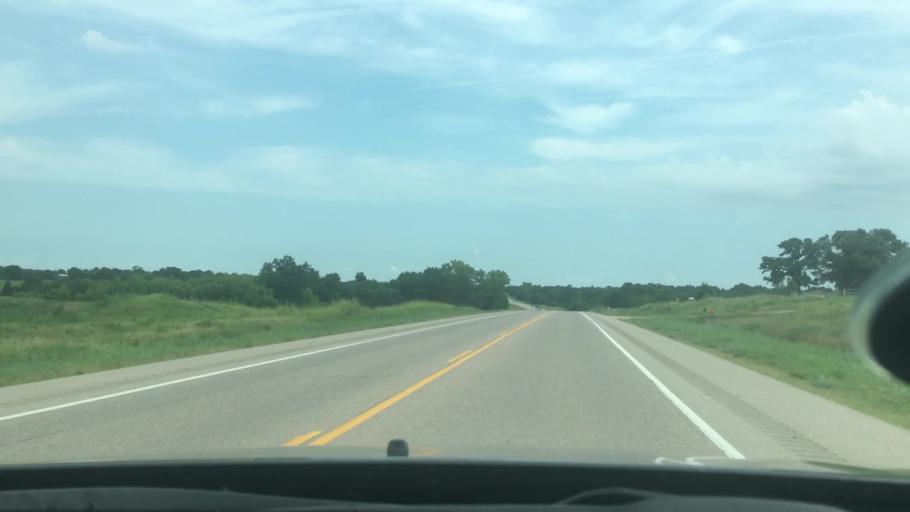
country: US
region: Oklahoma
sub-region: Seminole County
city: Seminole
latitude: 35.1703
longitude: -96.6741
